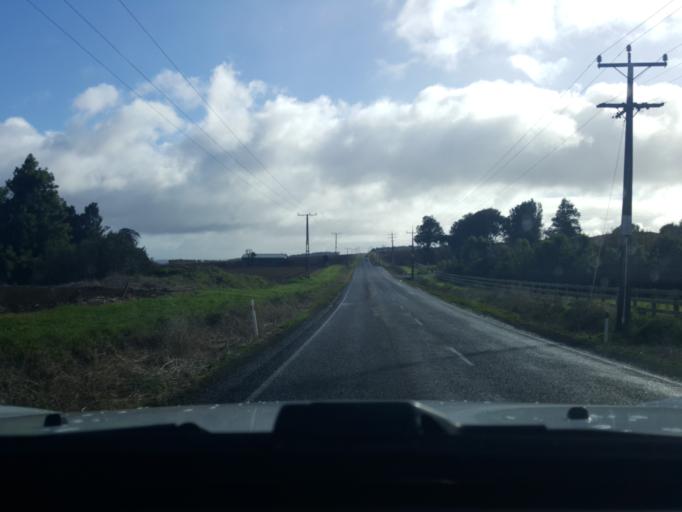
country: NZ
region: Auckland
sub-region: Auckland
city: Pukekohe East
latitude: -37.3259
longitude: 174.9863
